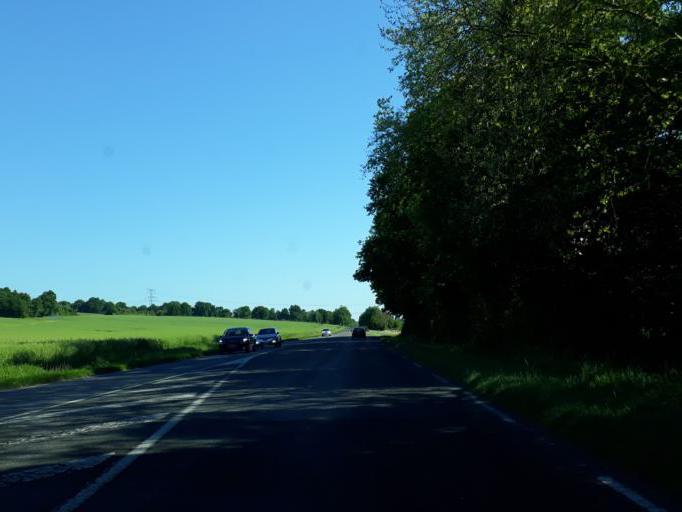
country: FR
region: Bourgogne
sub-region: Departement de la Nievre
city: Cosne-Cours-sur-Loire
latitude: 47.4691
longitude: 2.9298
